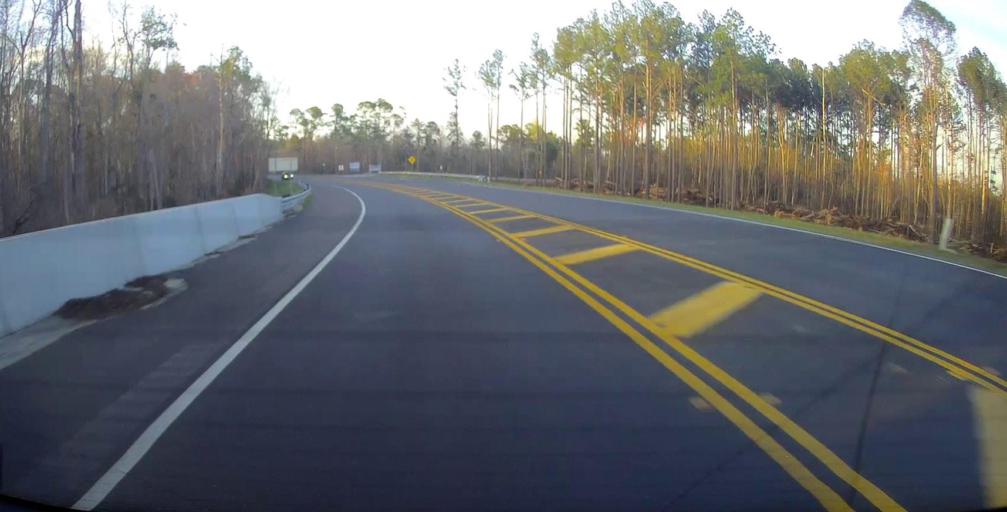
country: US
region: Georgia
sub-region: Chatham County
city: Bloomingdale
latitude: 32.1282
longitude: -81.3856
